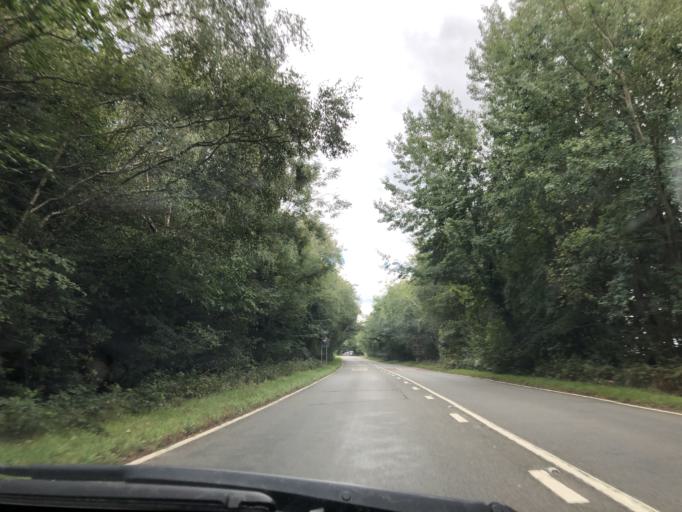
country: GB
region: England
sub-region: East Sussex
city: Forest Row
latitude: 51.0660
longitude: 0.0267
